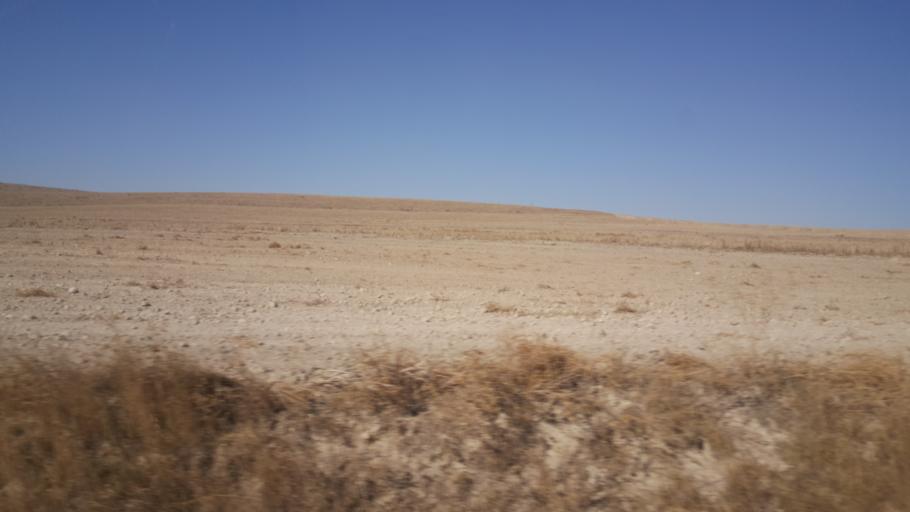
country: TR
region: Konya
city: Celtik
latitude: 39.0913
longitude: 32.0598
